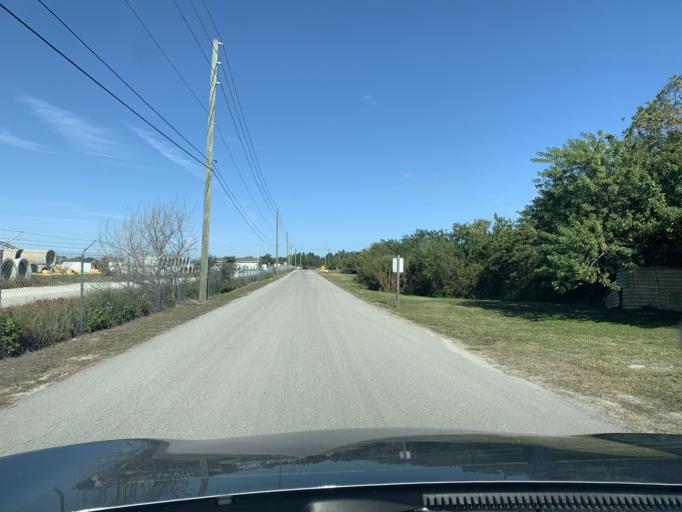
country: US
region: Florida
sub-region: Orange County
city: Lockhart
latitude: 28.6373
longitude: -81.4679
